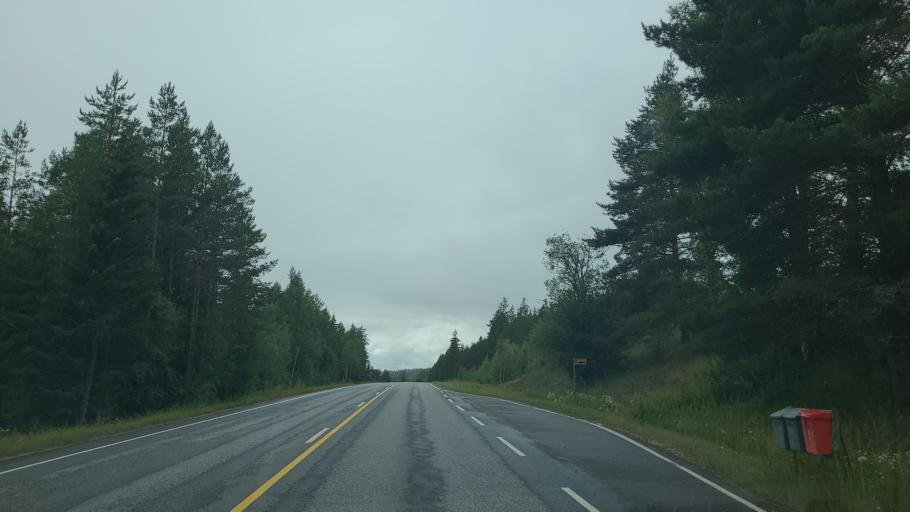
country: FI
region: Varsinais-Suomi
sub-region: Aboland-Turunmaa
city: Kimito
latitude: 60.1913
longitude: 22.6885
